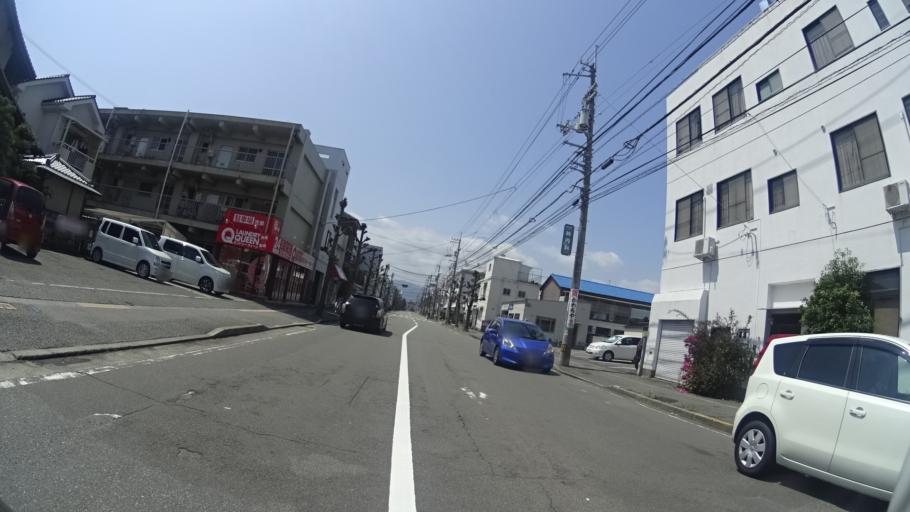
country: JP
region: Tokushima
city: Tokushima-shi
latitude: 34.0628
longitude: 134.5526
